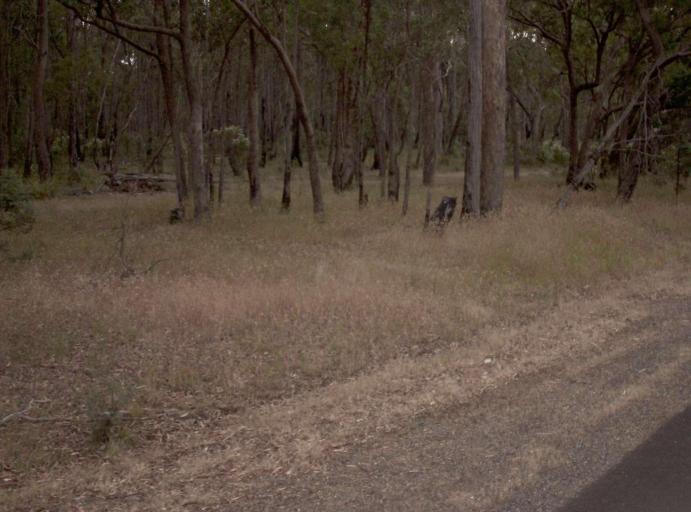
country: AU
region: Victoria
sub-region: Wellington
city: Sale
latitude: -38.4061
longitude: 146.9663
